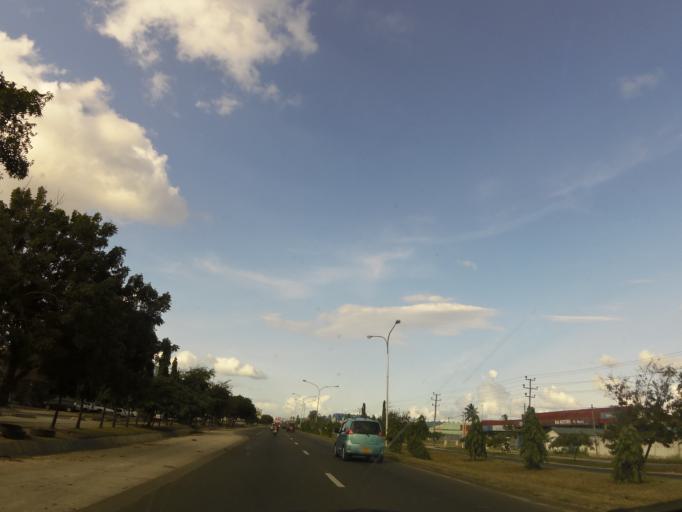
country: TZ
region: Dar es Salaam
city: Dar es Salaam
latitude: -6.8552
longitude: 39.2231
